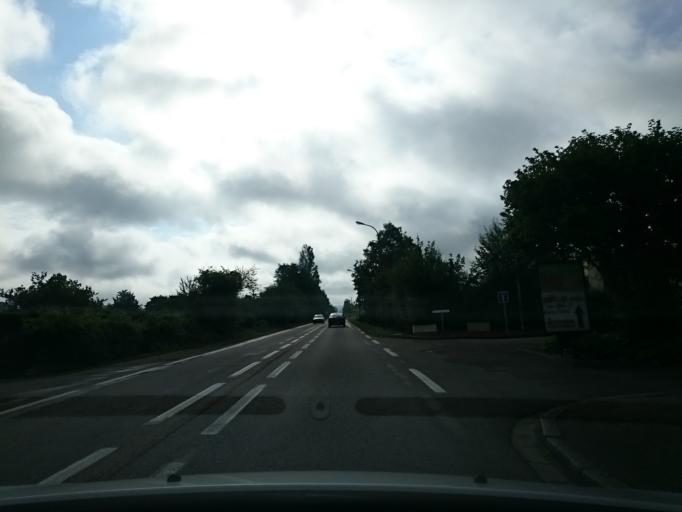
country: FR
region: Lower Normandy
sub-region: Departement du Calvados
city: Cambremer
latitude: 49.1180
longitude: 0.0187
